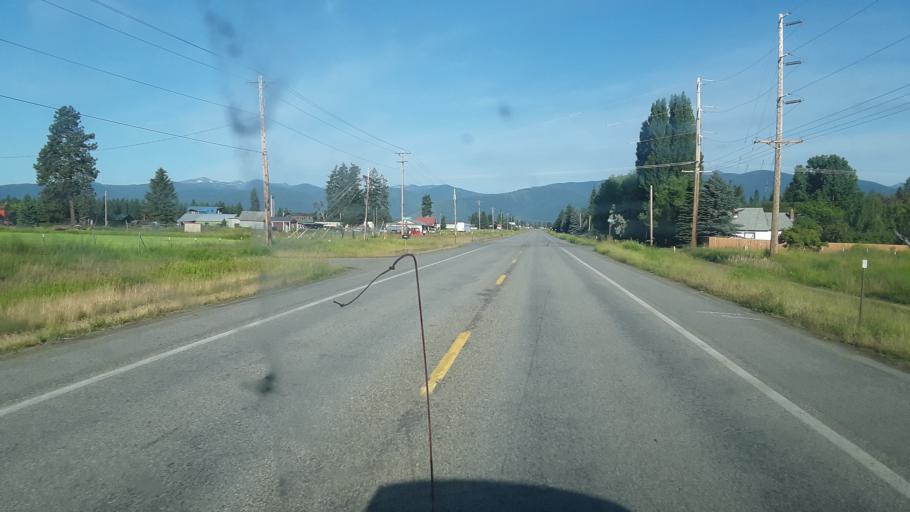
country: US
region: Idaho
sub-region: Boundary County
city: Bonners Ferry
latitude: 48.7315
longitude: -116.2748
